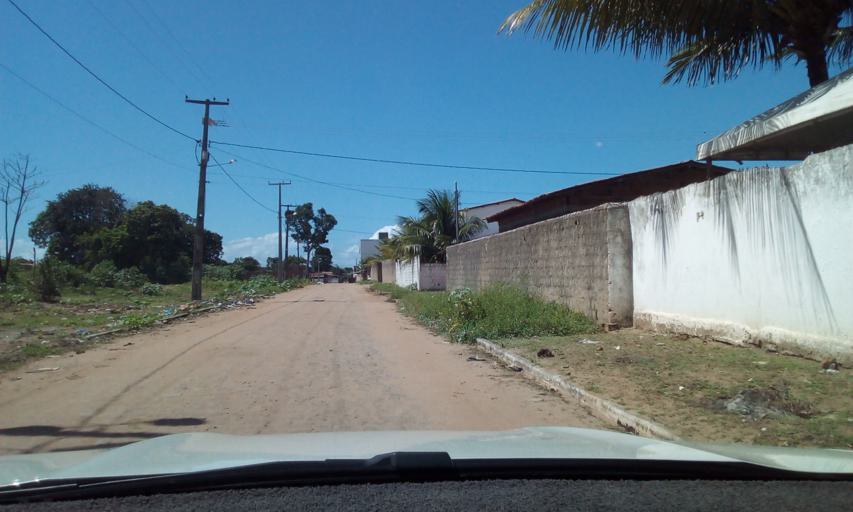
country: BR
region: Paraiba
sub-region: Joao Pessoa
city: Joao Pessoa
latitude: -7.1740
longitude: -34.8167
